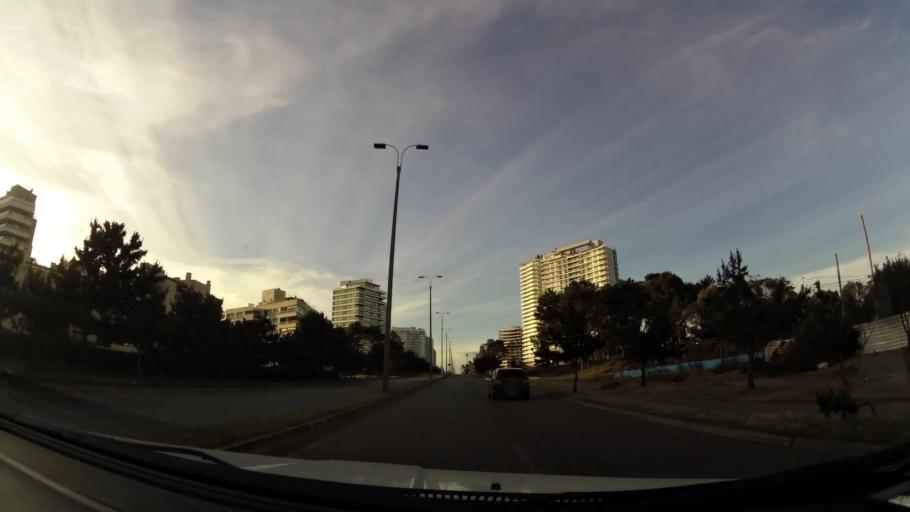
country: UY
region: Maldonado
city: Punta del Este
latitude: -34.9471
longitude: -54.9260
